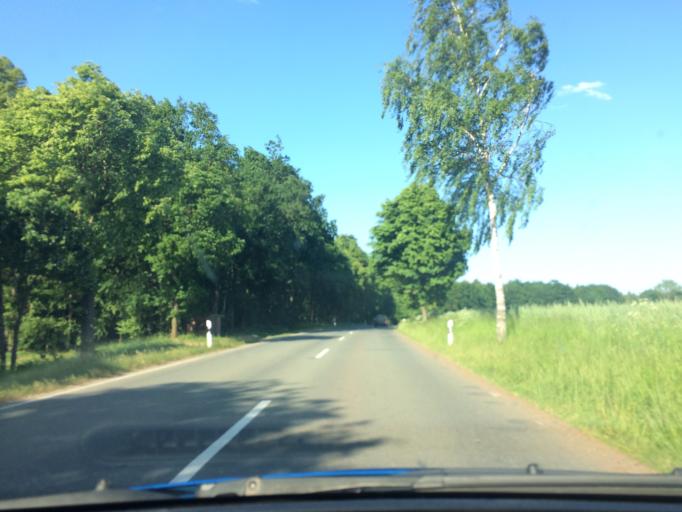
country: DE
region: Lower Saxony
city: Soltau
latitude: 53.0190
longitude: 9.8952
